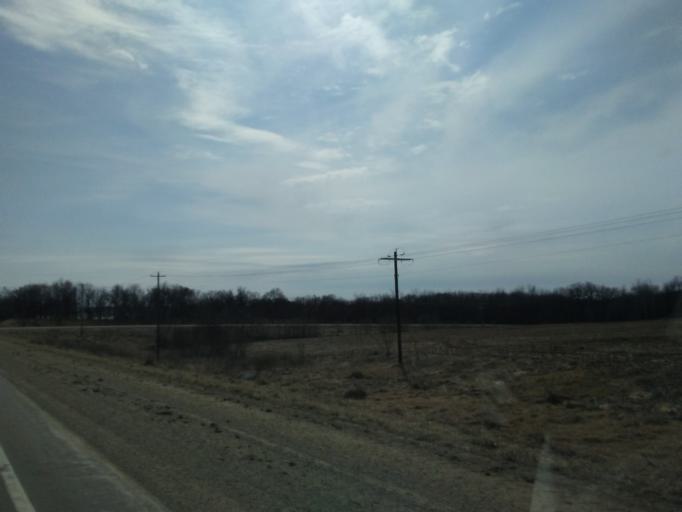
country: US
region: Iowa
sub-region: Winneshiek County
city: Decorah
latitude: 43.4303
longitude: -91.8599
